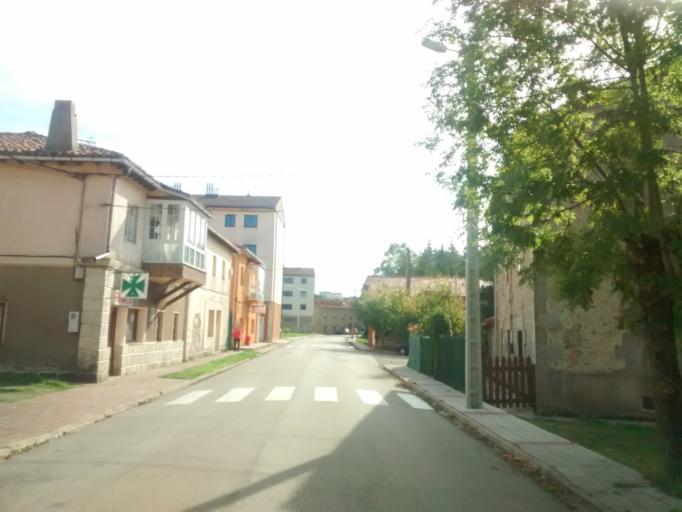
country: ES
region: Castille and Leon
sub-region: Provincia de Burgos
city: Arija
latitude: 42.9941
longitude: -3.9454
